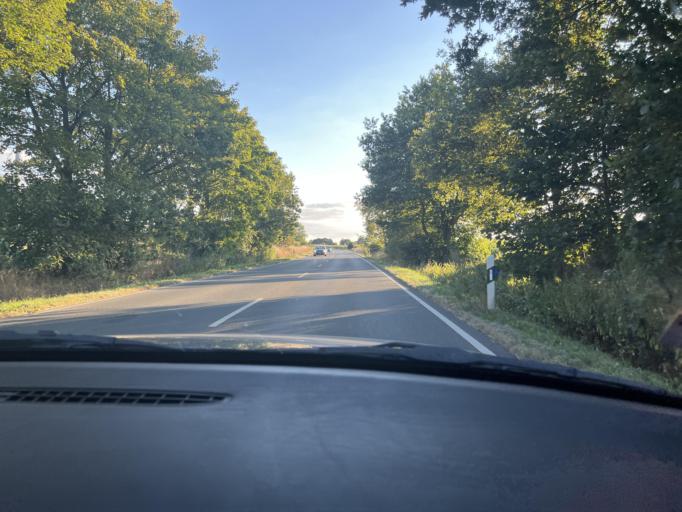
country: DE
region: Schleswig-Holstein
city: Linden
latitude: 54.2529
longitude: 9.1762
